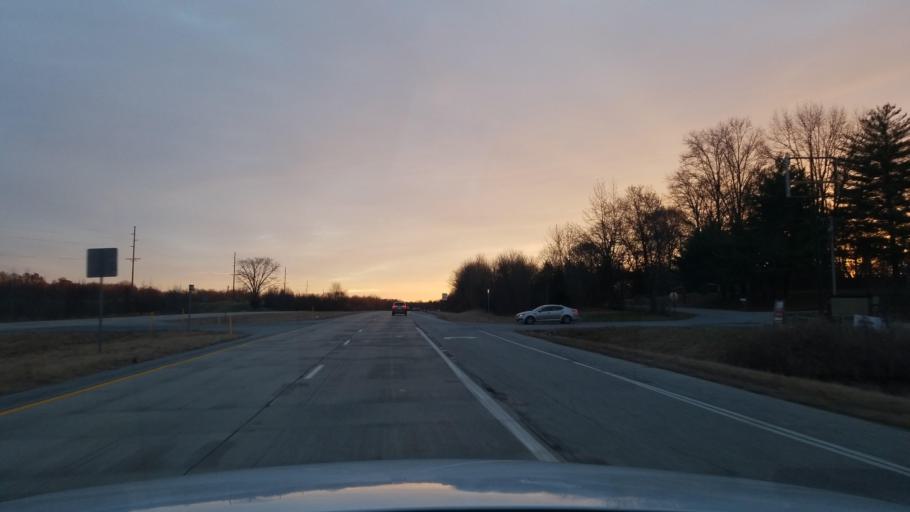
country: US
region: Indiana
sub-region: Posey County
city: Mount Vernon
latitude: 37.9423
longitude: -87.7312
